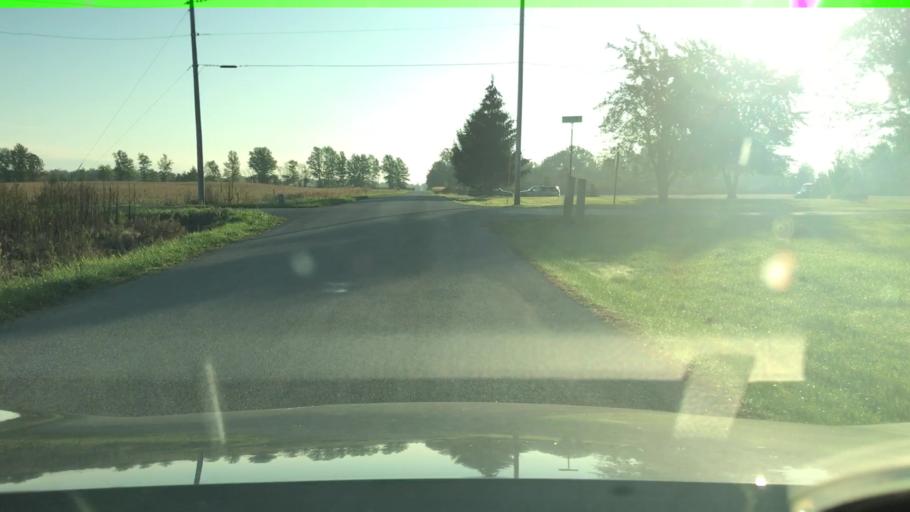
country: US
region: Indiana
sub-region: Jay County
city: Dunkirk
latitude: 40.4065
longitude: -85.2580
